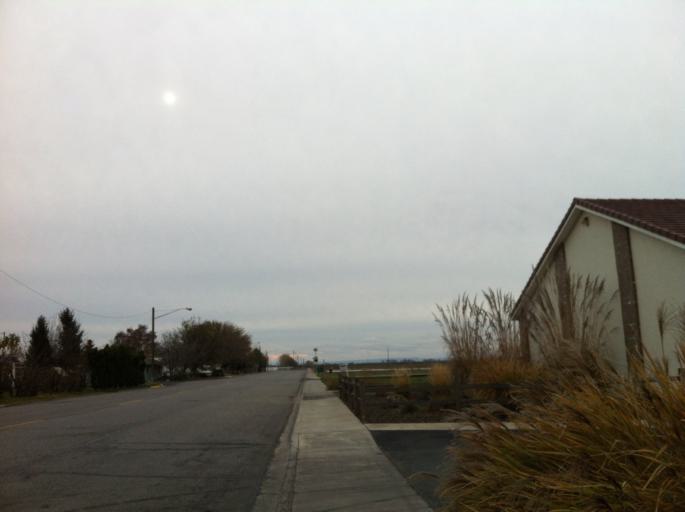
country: US
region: Washington
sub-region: Grant County
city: Quincy
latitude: 47.2293
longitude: -119.8641
